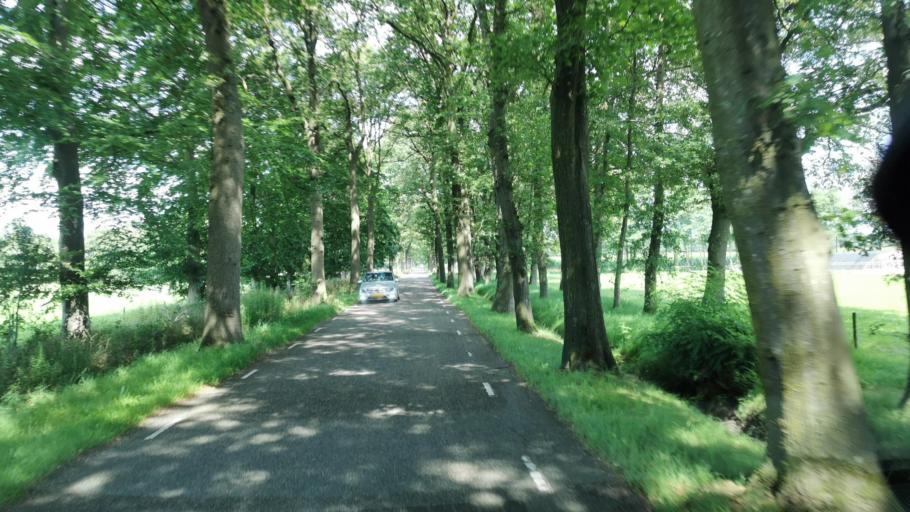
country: NL
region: Overijssel
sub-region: Gemeente Enschede
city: Enschede
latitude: 52.1737
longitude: 6.8554
